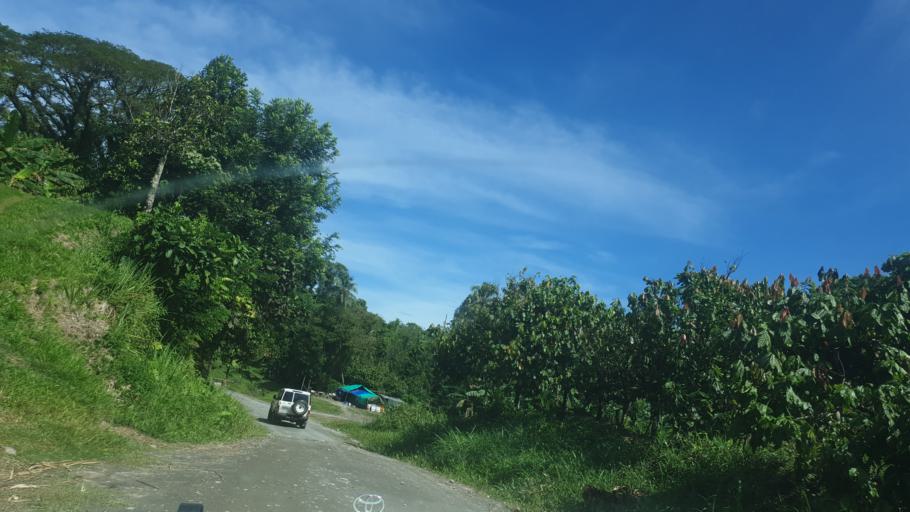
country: PG
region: Bougainville
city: Panguna
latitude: -6.5024
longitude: 155.3286
